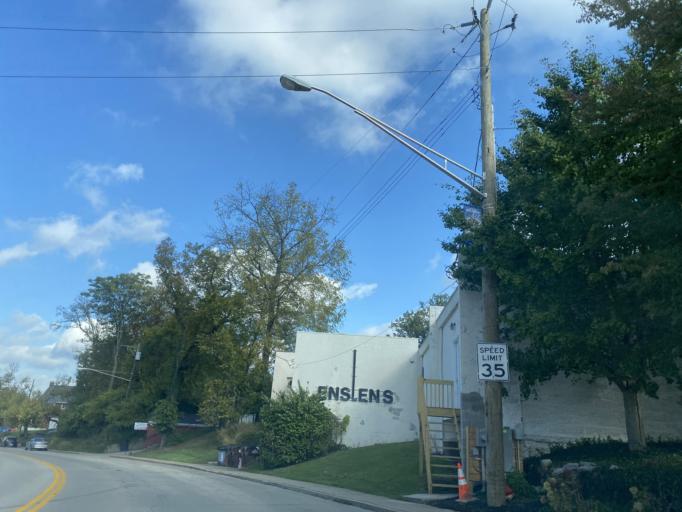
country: US
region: Kentucky
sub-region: Campbell County
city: Fort Thomas
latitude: 39.0874
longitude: -84.4487
